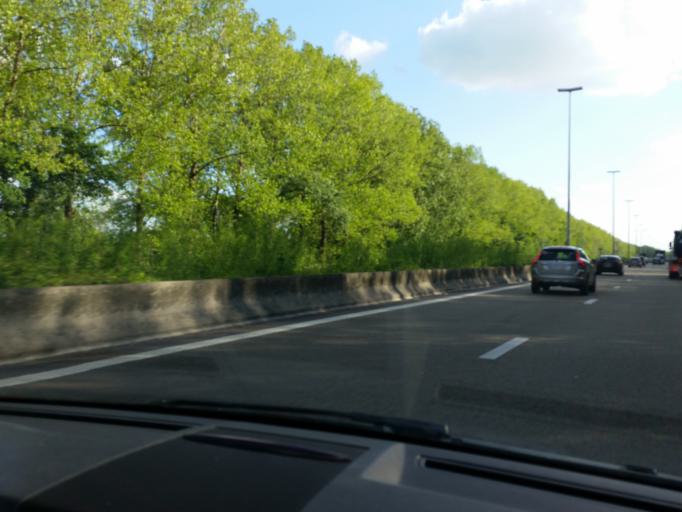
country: BE
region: Flanders
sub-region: Provincie Oost-Vlaanderen
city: Waasmunster
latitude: 51.1164
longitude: 4.0627
